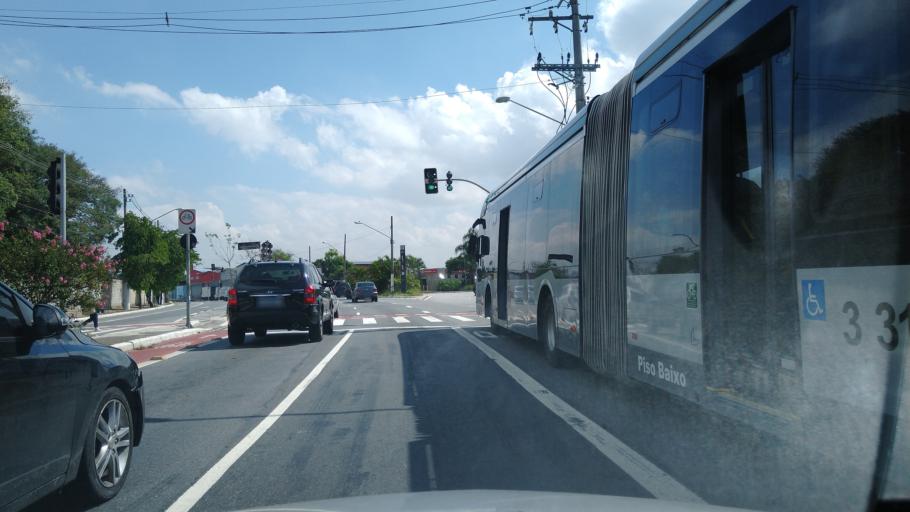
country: BR
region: Sao Paulo
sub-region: Guarulhos
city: Guarulhos
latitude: -23.4857
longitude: -46.5019
